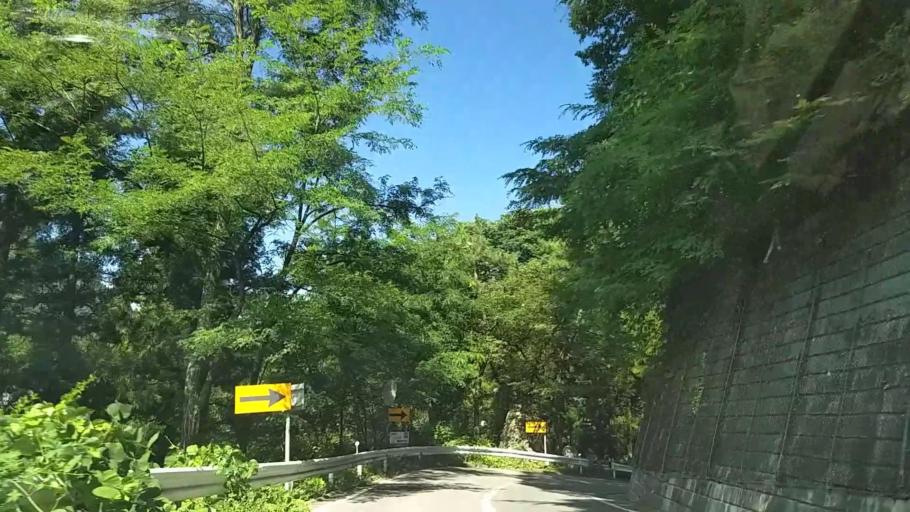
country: JP
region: Nagano
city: Matsumoto
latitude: 36.2204
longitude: 138.0420
